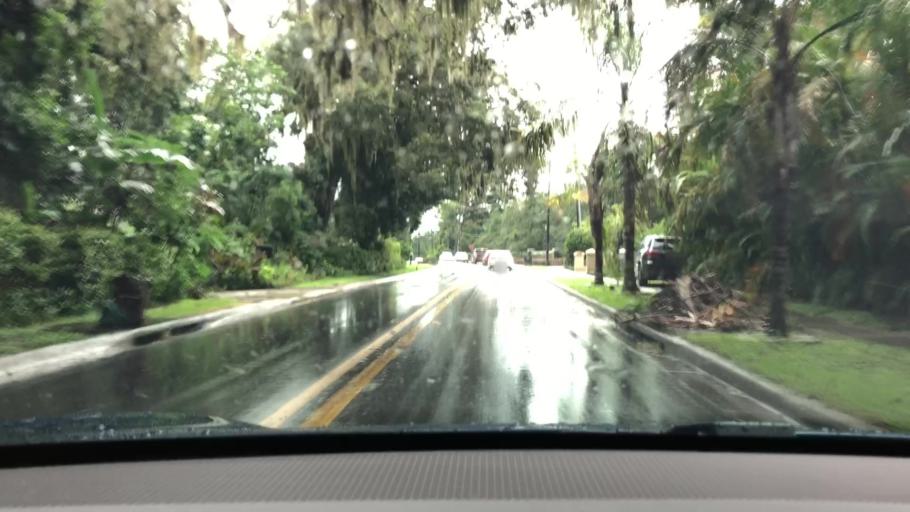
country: US
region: Florida
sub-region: Orange County
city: Edgewood
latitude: 28.4942
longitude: -81.3688
